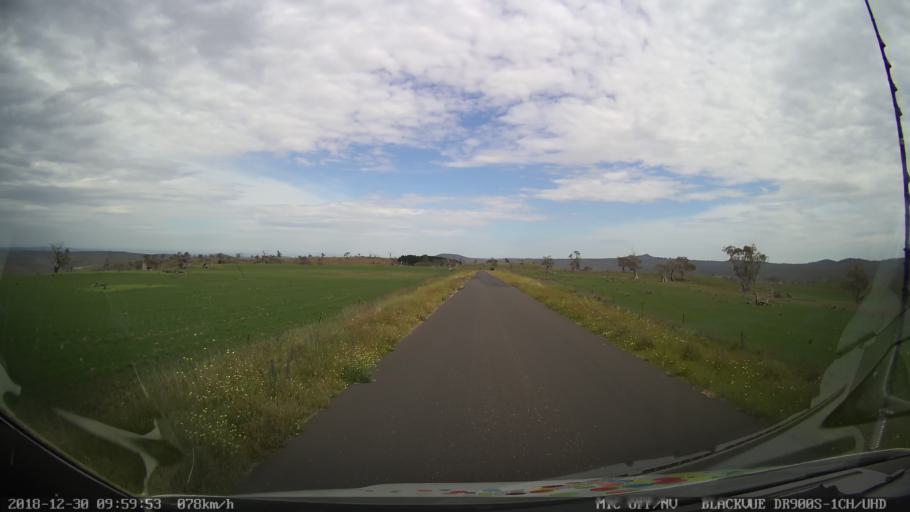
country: AU
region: New South Wales
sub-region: Cooma-Monaro
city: Cooma
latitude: -36.5206
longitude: 149.2044
